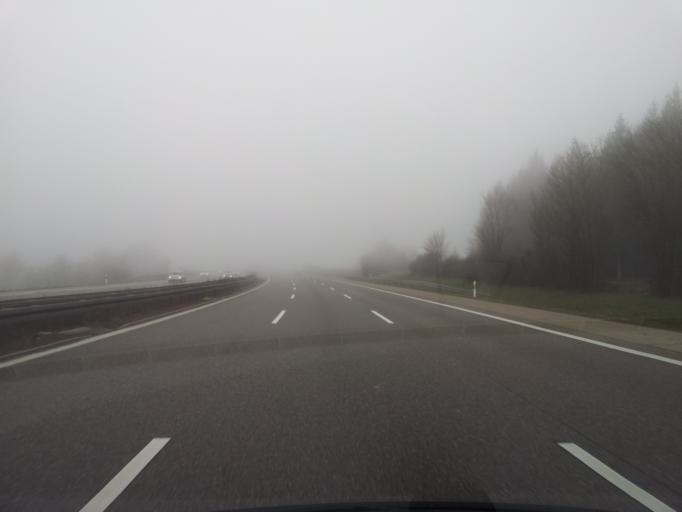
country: DE
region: Baden-Wuerttemberg
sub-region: Freiburg Region
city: Engen
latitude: 47.8912
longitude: 8.7674
